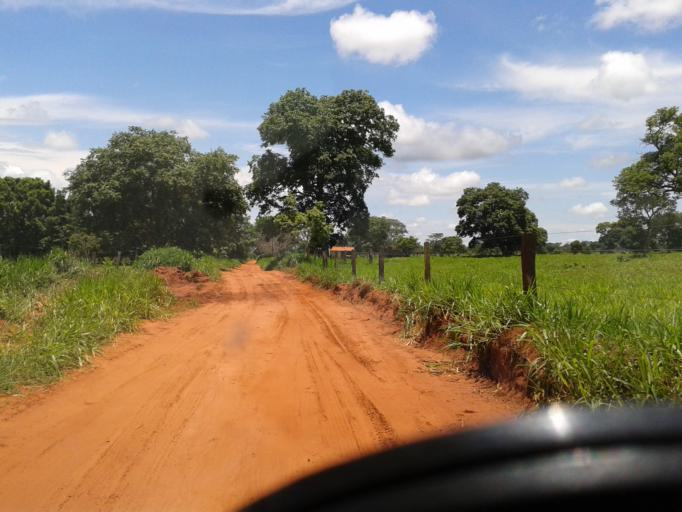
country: BR
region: Minas Gerais
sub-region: Santa Vitoria
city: Santa Vitoria
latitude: -18.9495
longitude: -49.8629
